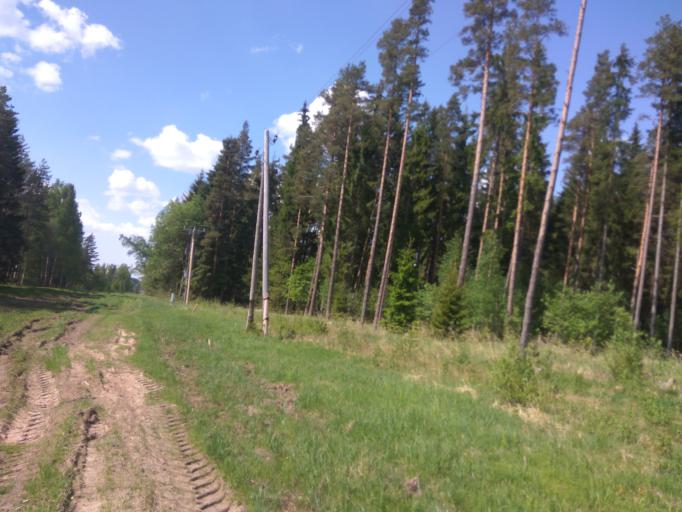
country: LV
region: Kuldigas Rajons
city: Kuldiga
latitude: 57.1864
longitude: 21.9907
